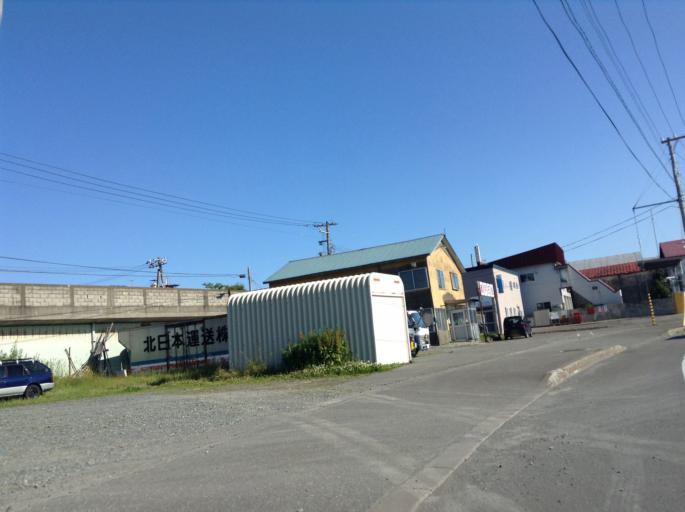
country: JP
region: Hokkaido
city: Wakkanai
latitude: 45.4104
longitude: 141.6769
